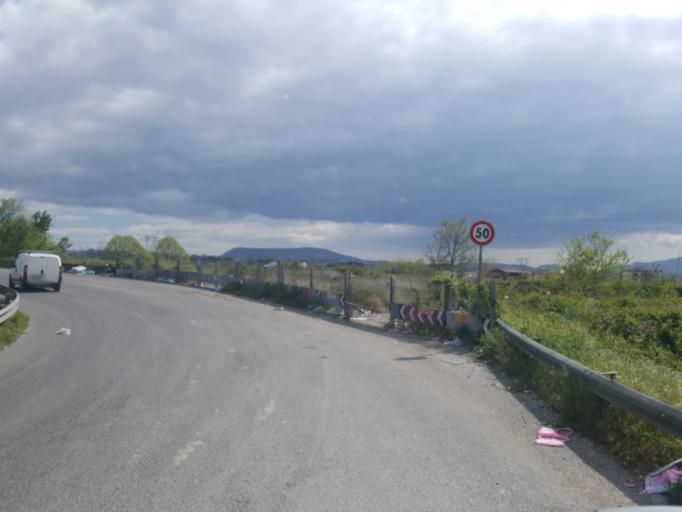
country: IT
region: Campania
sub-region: Provincia di Napoli
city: Torretta-Scalzapecora
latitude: 40.9321
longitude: 14.1218
